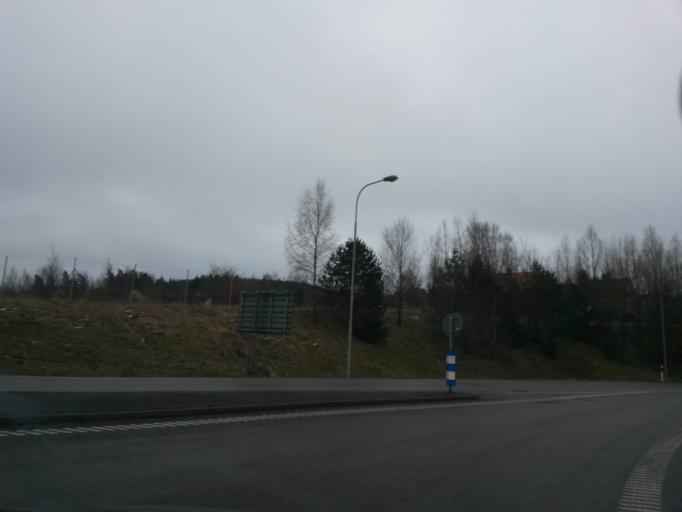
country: SE
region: Vaestra Goetaland
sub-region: Marks Kommun
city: Kinna
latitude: 57.4806
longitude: 12.6568
